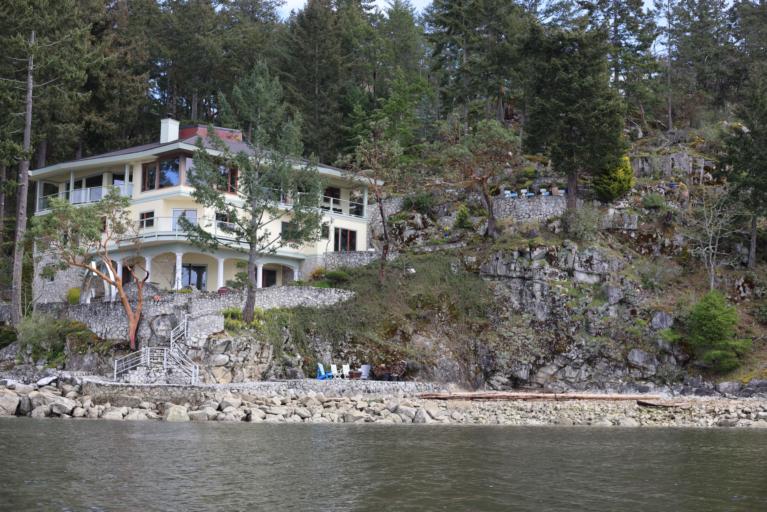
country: CA
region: British Columbia
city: North Saanich
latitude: 48.6042
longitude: -123.4815
